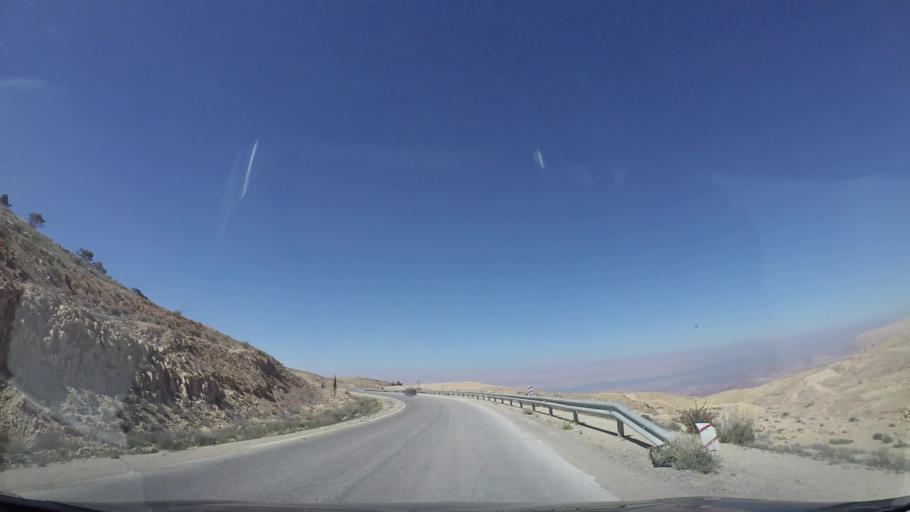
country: JO
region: Tafielah
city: At Tafilah
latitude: 30.8585
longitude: 35.5428
